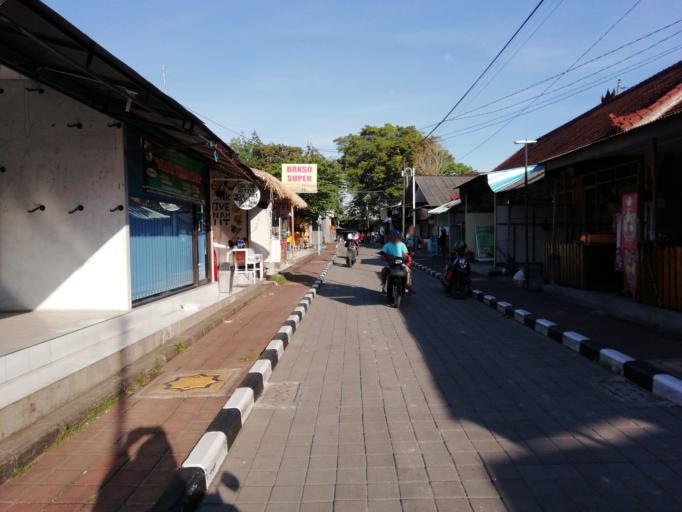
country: ID
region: Bali
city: Banjar Batanbuah
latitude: -8.6177
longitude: 115.0879
